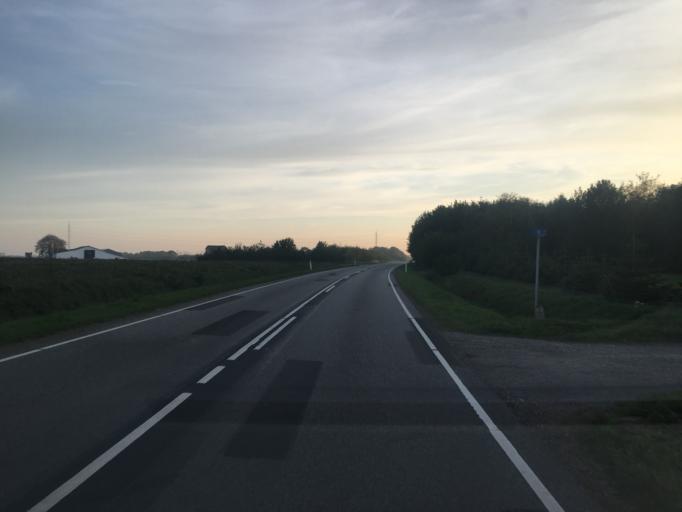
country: DK
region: South Denmark
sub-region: Tonder Kommune
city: Logumkloster
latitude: 55.0458
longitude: 9.0925
